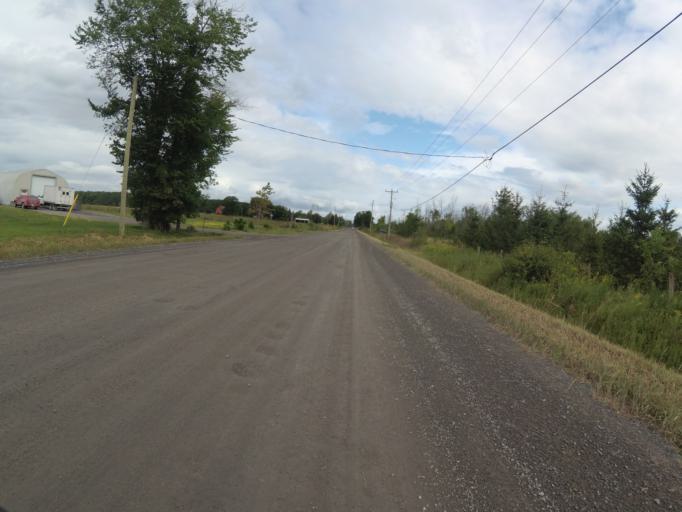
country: CA
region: Ontario
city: Clarence-Rockland
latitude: 45.4628
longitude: -75.2992
